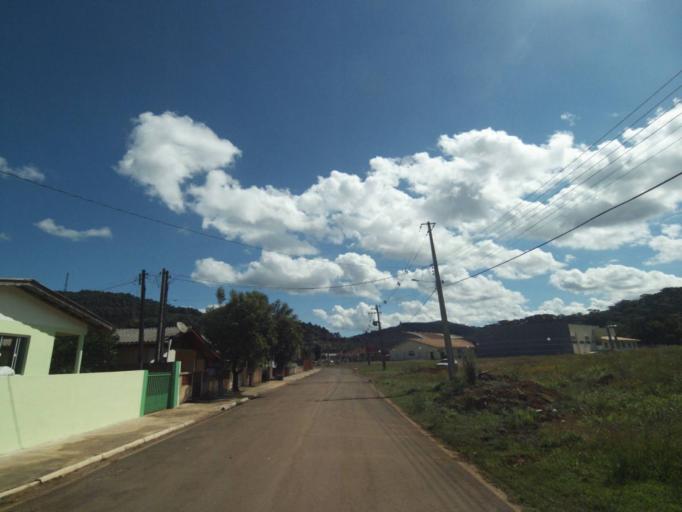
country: BR
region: Parana
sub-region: Uniao Da Vitoria
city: Uniao da Vitoria
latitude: -26.1498
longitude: -51.5469
